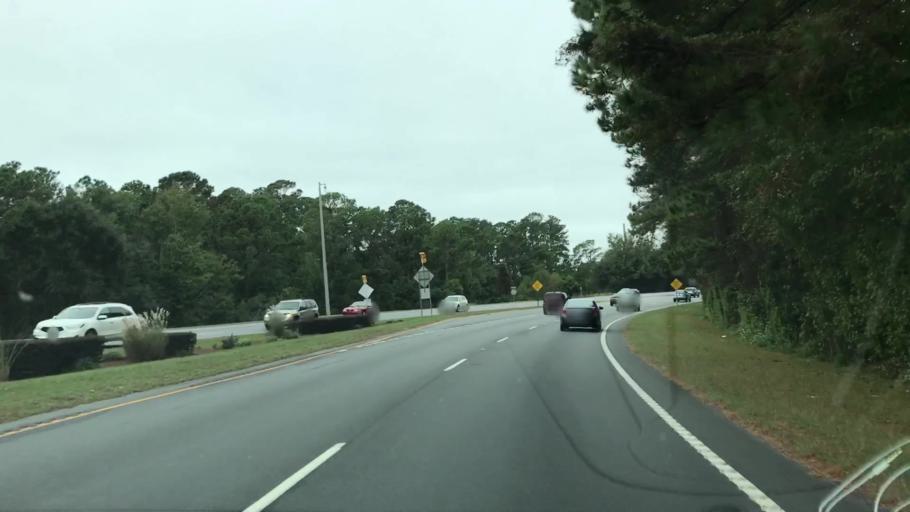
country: US
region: South Carolina
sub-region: Beaufort County
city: Hilton Head Island
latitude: 32.2187
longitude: -80.7753
